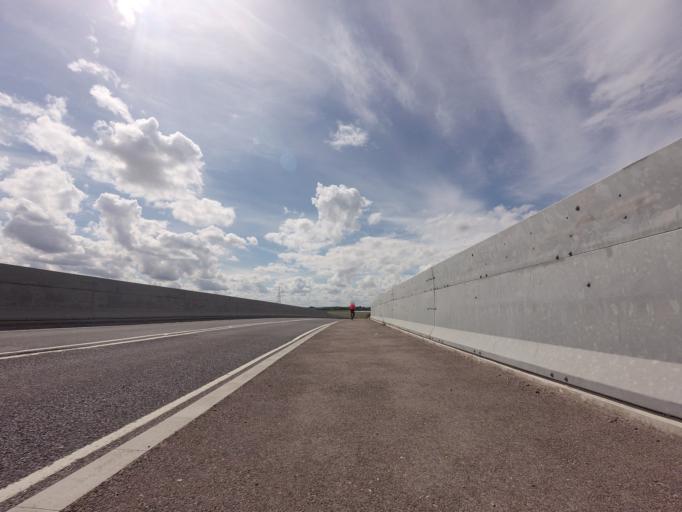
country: GB
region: England
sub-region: Medway
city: Allhallows
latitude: 51.4490
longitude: 0.6494
